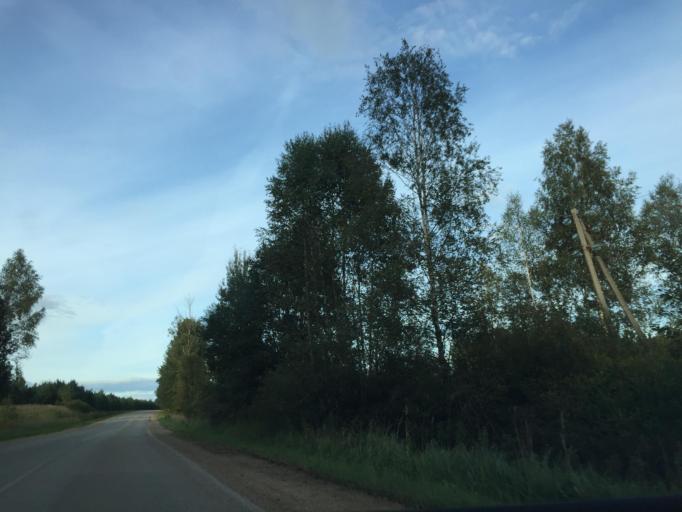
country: LV
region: Viesite
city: Viesite
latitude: 56.3161
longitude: 25.4528
